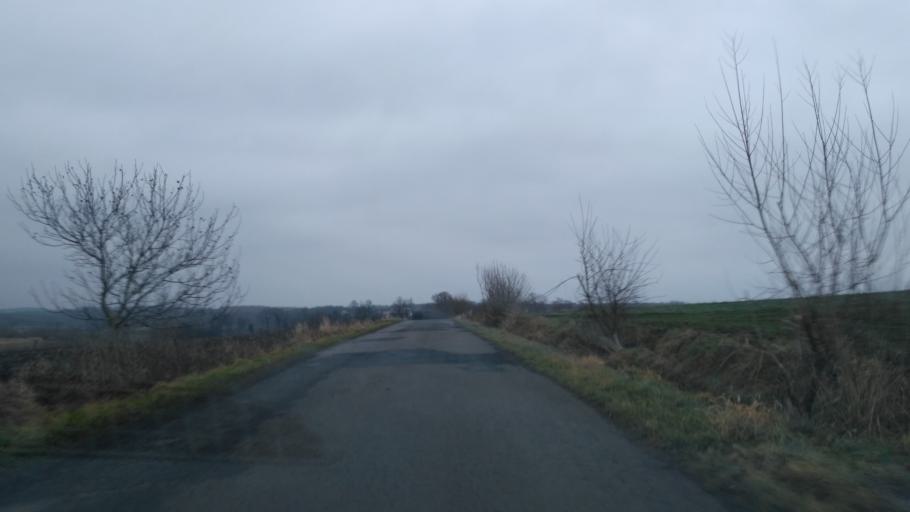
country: PL
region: Subcarpathian Voivodeship
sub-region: Powiat jaroslawski
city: Pruchnik
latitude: 49.9358
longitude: 22.5476
